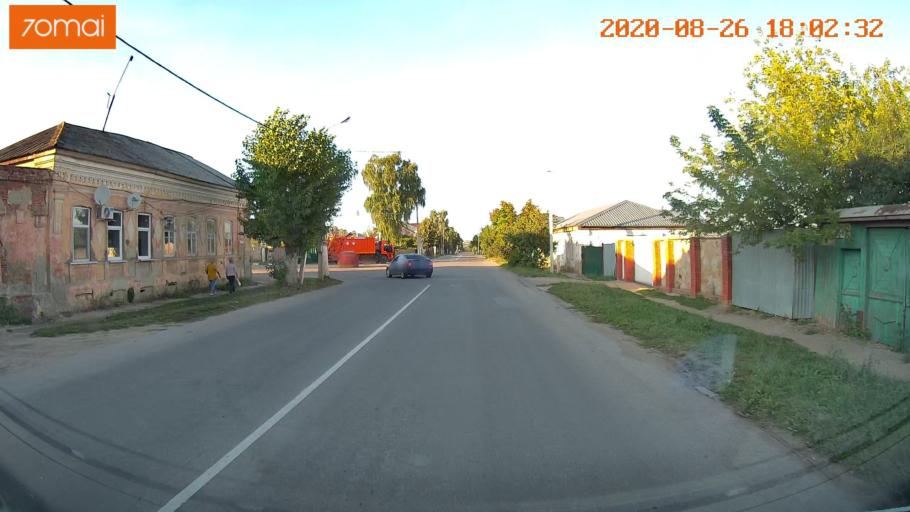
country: RU
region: Tula
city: Yefremov
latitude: 53.1395
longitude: 38.1212
